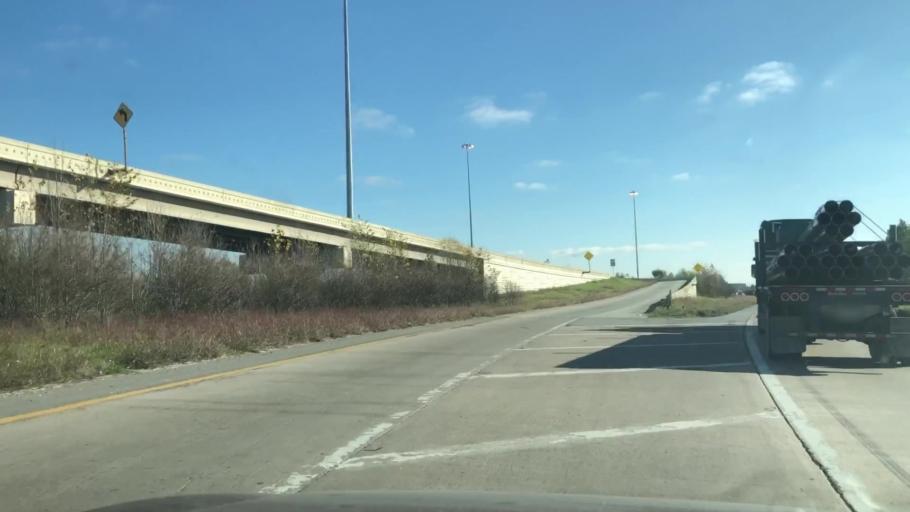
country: US
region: Texas
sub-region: Harris County
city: Jacinto City
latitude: 29.7736
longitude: -95.2619
